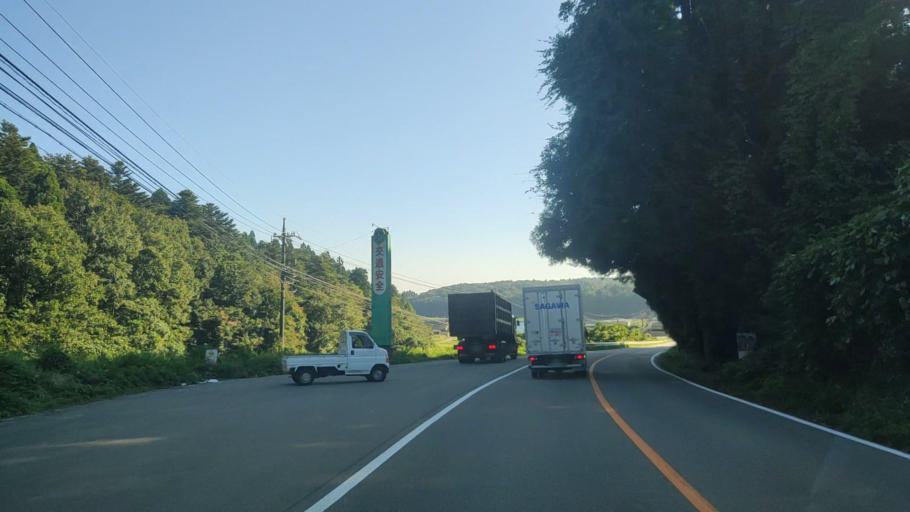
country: JP
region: Ishikawa
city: Nanao
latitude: 37.2077
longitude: 136.9086
